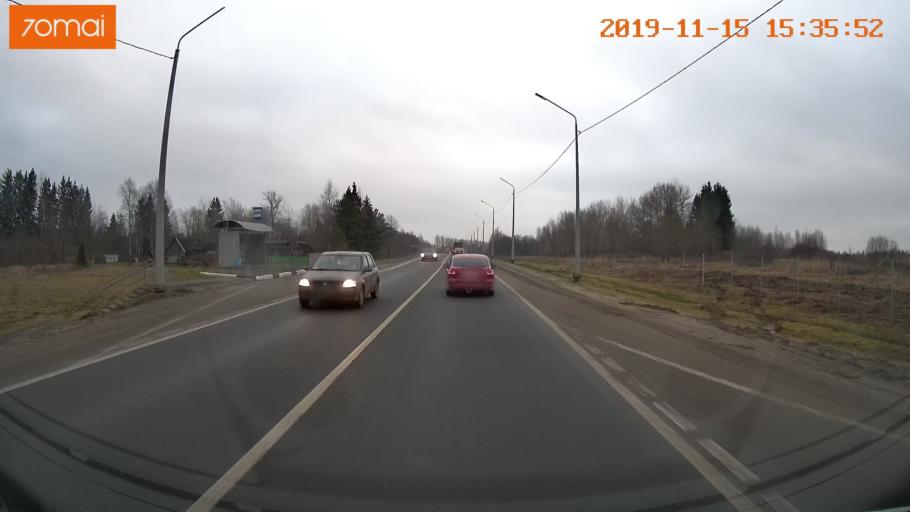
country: RU
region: Jaroslavl
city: Danilov
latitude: 58.0550
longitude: 40.0883
